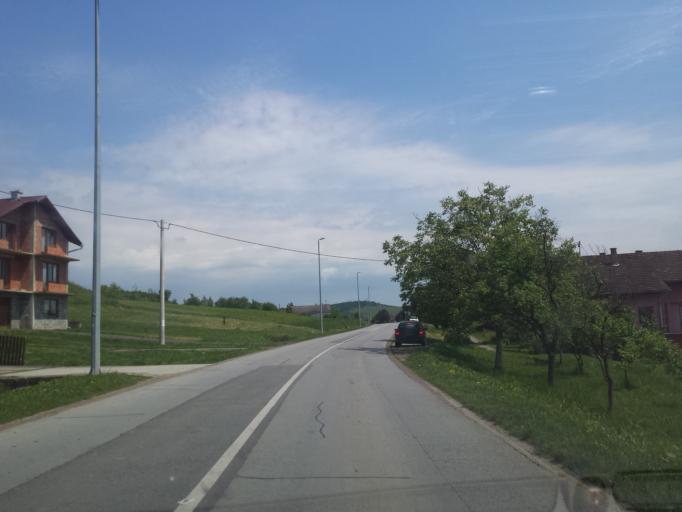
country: HR
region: Brodsko-Posavska
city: Oriovac
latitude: 45.1609
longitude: 17.7850
